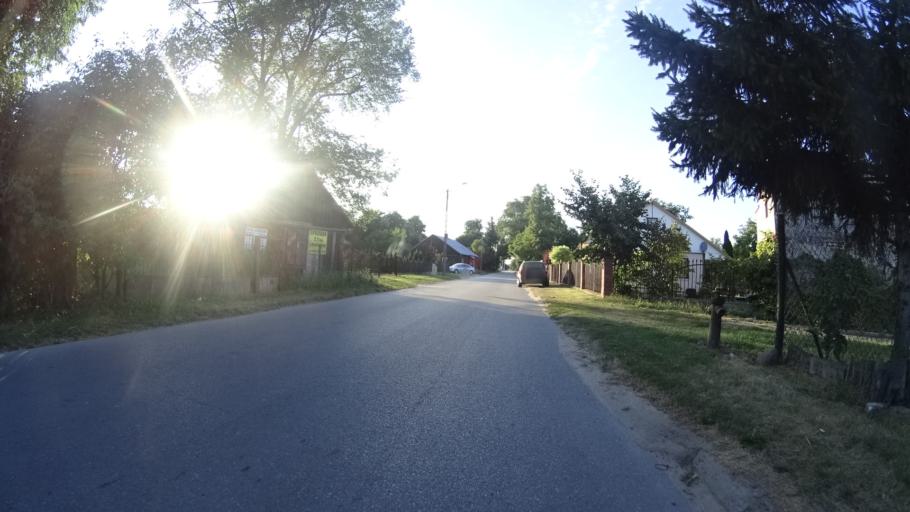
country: PL
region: Masovian Voivodeship
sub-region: Powiat grojecki
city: Goszczyn
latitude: 51.6937
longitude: 20.8161
